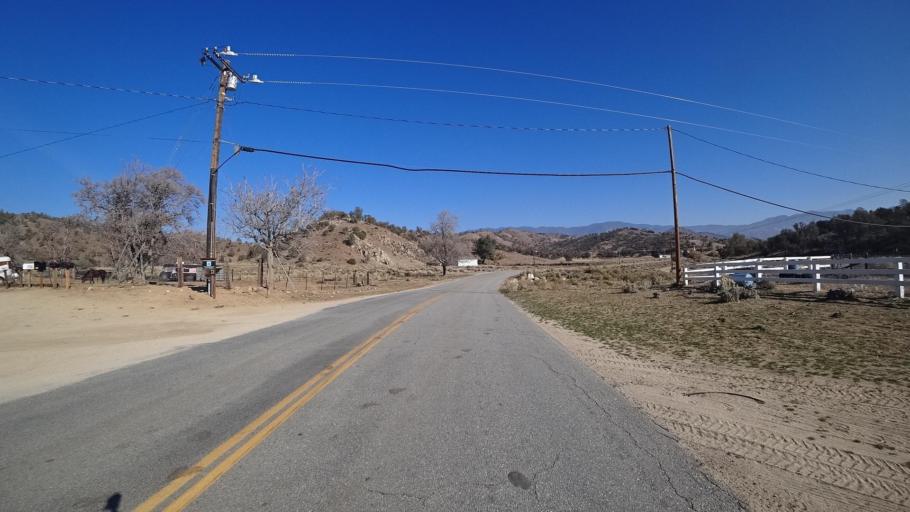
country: US
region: California
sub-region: Kern County
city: Tehachapi
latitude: 35.3092
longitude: -118.4199
